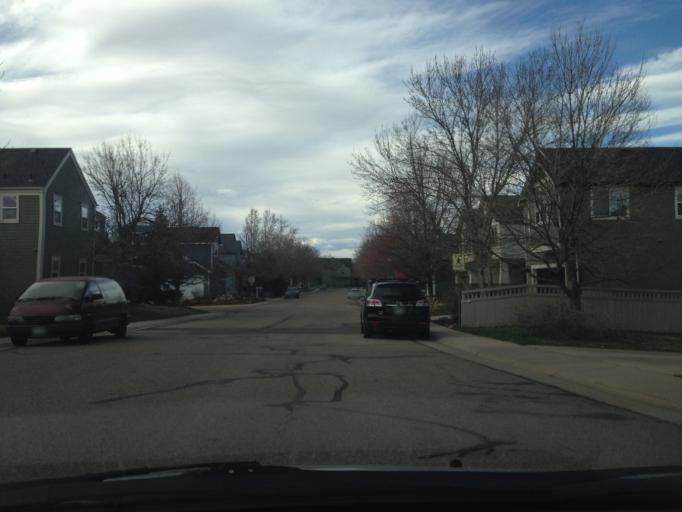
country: US
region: Colorado
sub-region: Boulder County
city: Louisville
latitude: 39.9971
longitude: -105.1158
